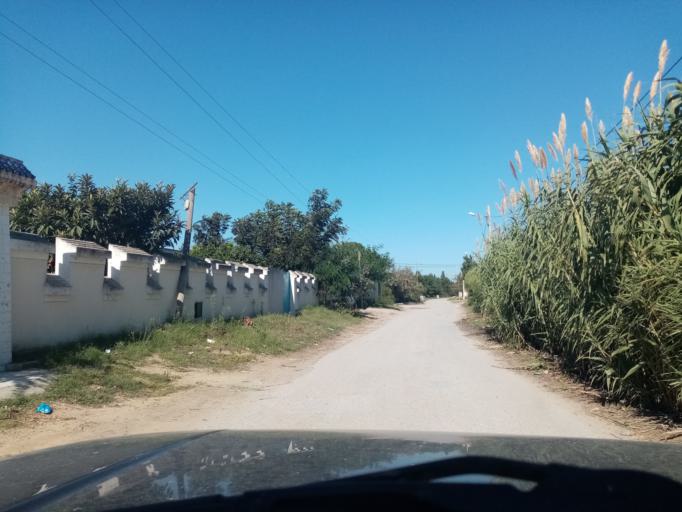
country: TN
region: Nabul
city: Bu `Urqub
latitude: 36.5717
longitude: 10.5752
